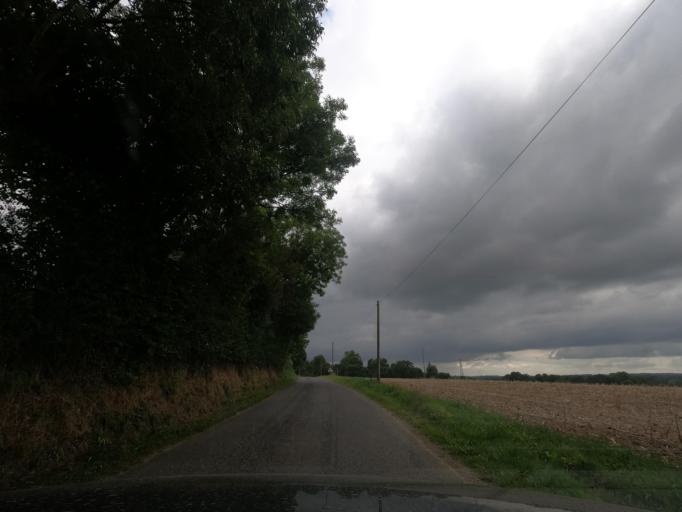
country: FR
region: Lower Normandy
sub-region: Departement de l'Orne
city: Briouze
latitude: 48.7165
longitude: -0.3267
